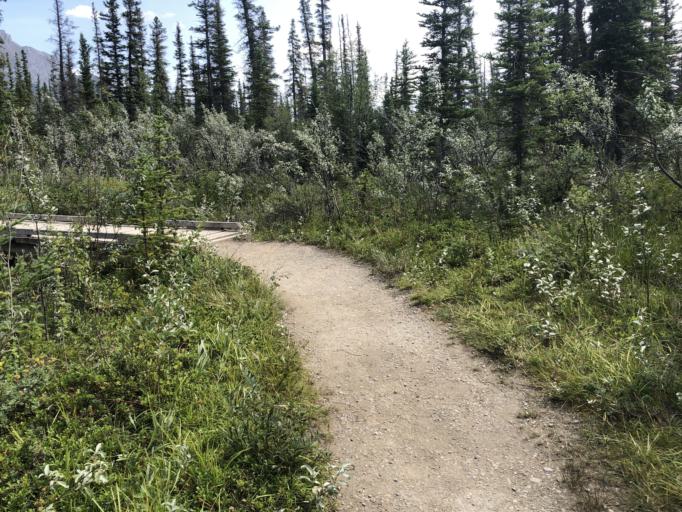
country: CA
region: Alberta
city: Jasper Park Lodge
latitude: 53.1459
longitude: -117.9804
